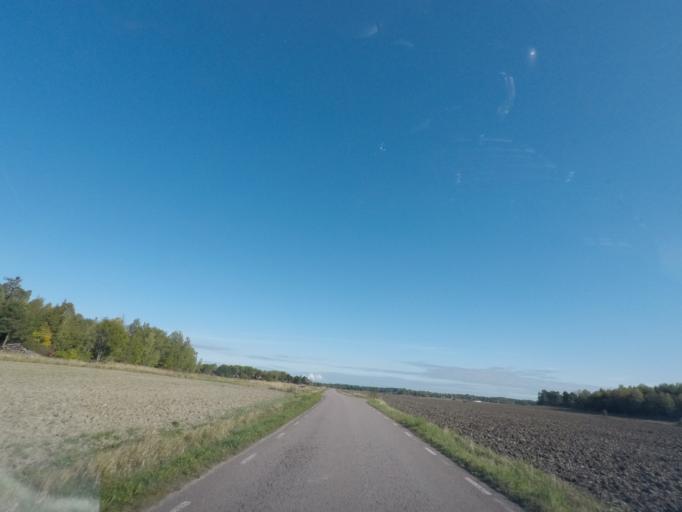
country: SE
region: Soedermanland
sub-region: Eskilstuna Kommun
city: Kvicksund
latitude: 59.5507
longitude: 16.4094
